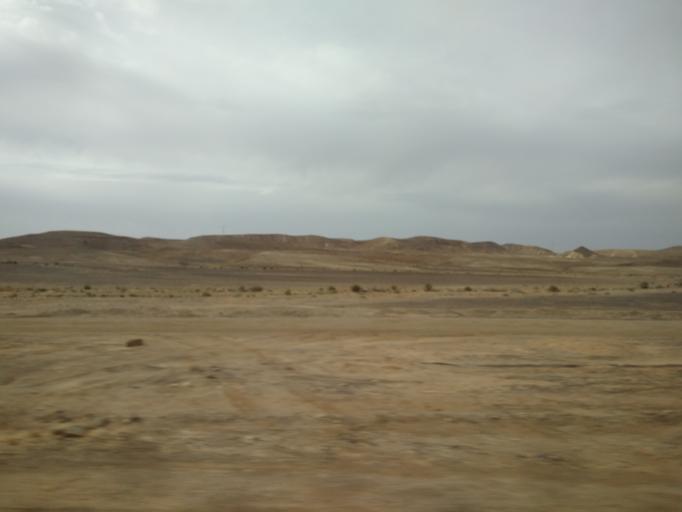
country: IL
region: Southern District
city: Eilat
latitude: 29.9172
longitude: 34.8819
